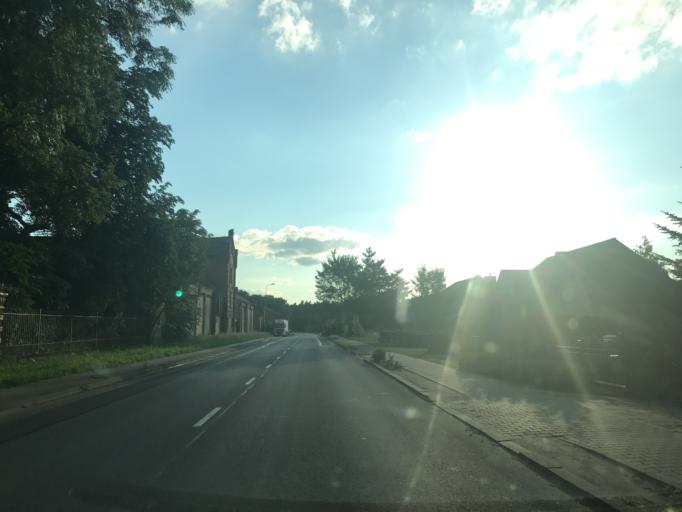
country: PL
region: Greater Poland Voivodeship
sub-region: Powiat jarocinski
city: Jaraczewo
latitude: 51.9771
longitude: 17.3642
